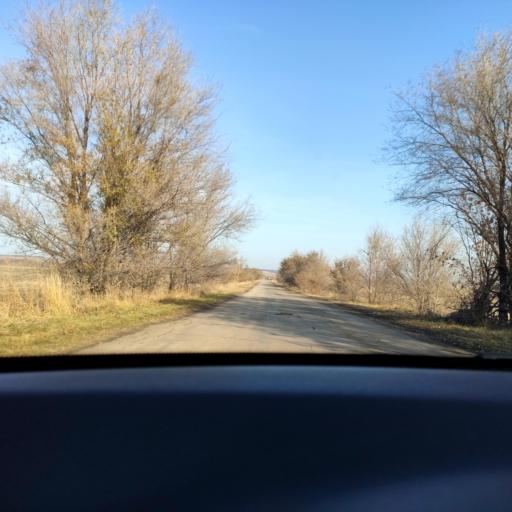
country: RU
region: Samara
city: Krasnoarmeyskoye
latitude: 52.8902
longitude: 50.0117
